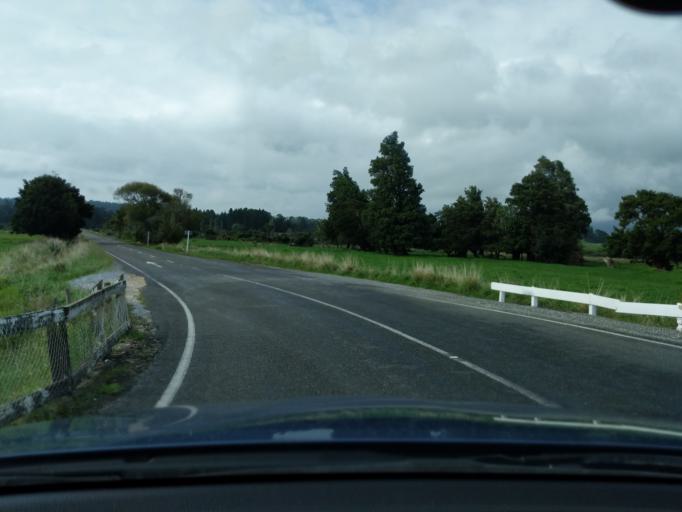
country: NZ
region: Tasman
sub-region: Tasman District
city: Takaka
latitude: -40.6761
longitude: 172.6613
